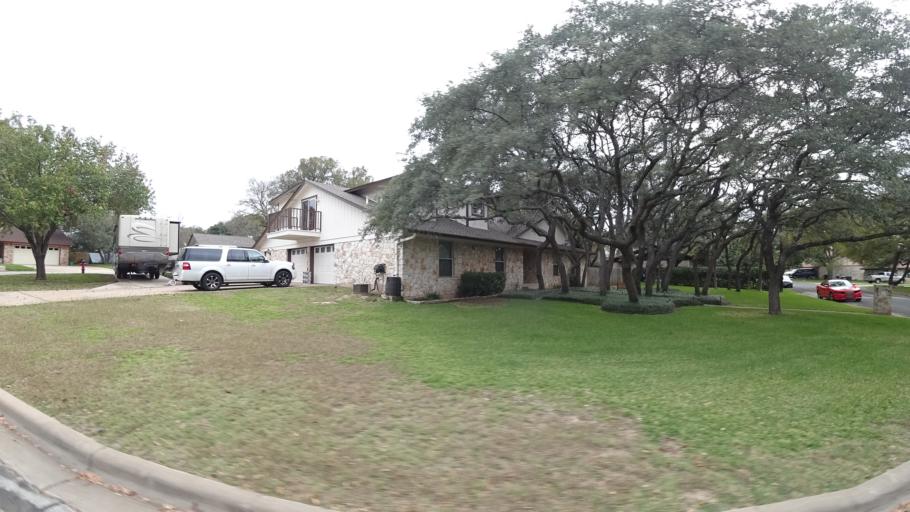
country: US
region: Texas
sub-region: Williamson County
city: Round Rock
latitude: 30.5021
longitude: -97.6904
